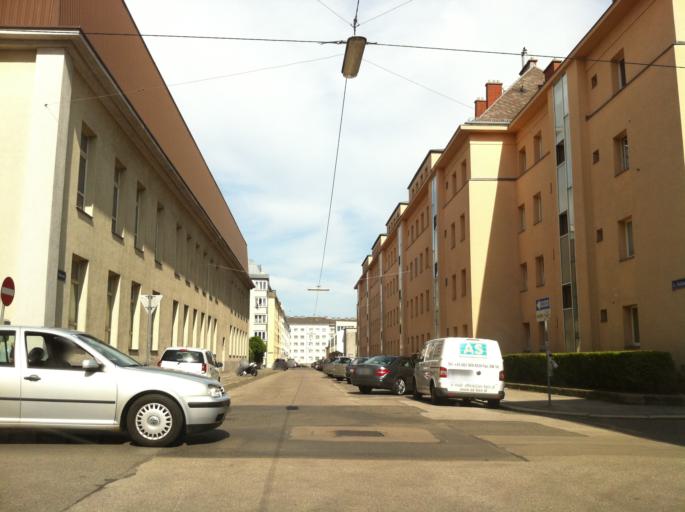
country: AT
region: Vienna
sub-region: Wien Stadt
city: Vienna
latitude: 48.1950
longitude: 16.2936
